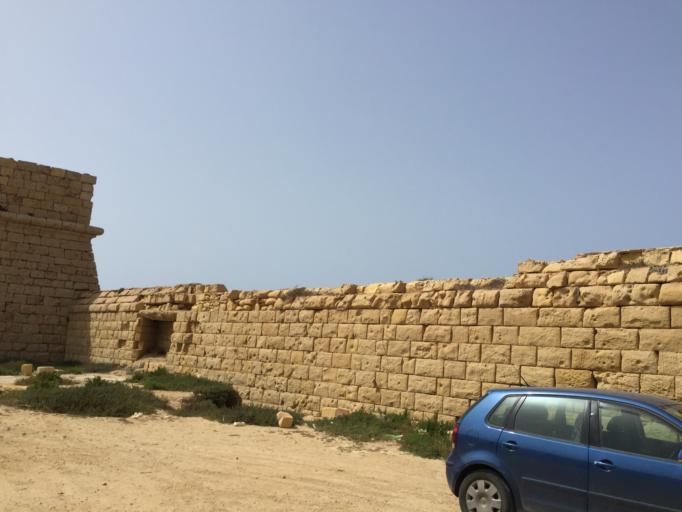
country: MT
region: Il-Kalkara
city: Kalkara
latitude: 35.8972
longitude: 14.5296
